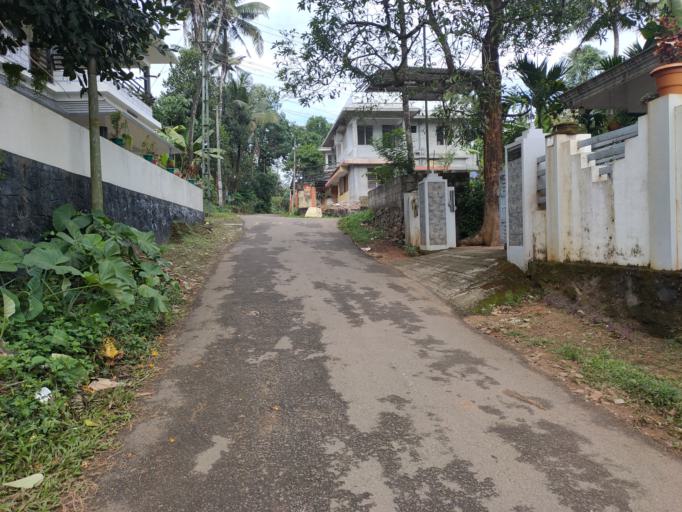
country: IN
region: Kerala
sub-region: Ernakulam
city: Kotamangalam
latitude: 10.0044
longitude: 76.6446
